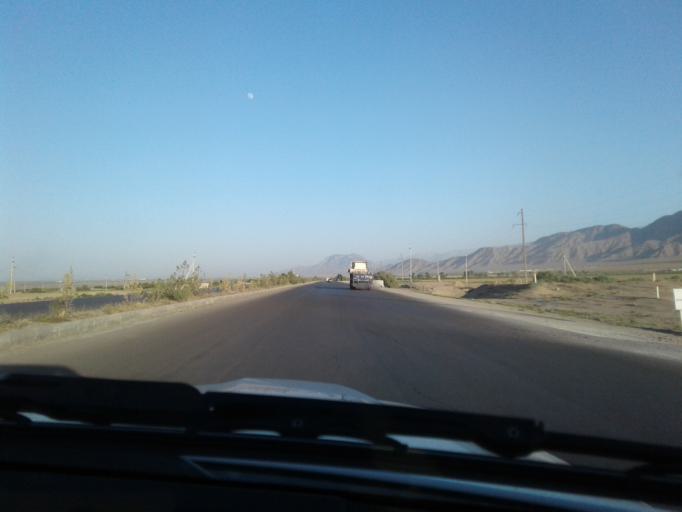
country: TM
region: Ahal
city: Baharly
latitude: 38.2239
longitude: 57.7967
